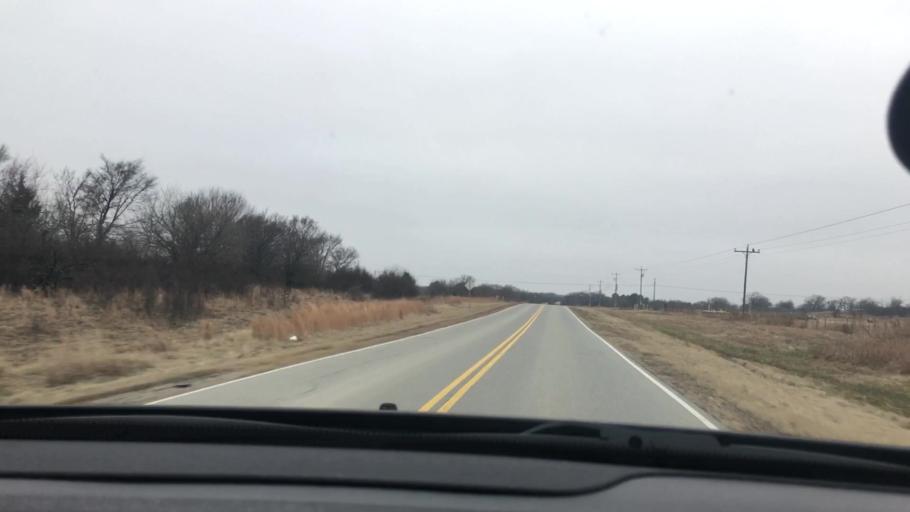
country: US
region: Oklahoma
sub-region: Coal County
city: Coalgate
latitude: 34.5092
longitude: -96.2954
